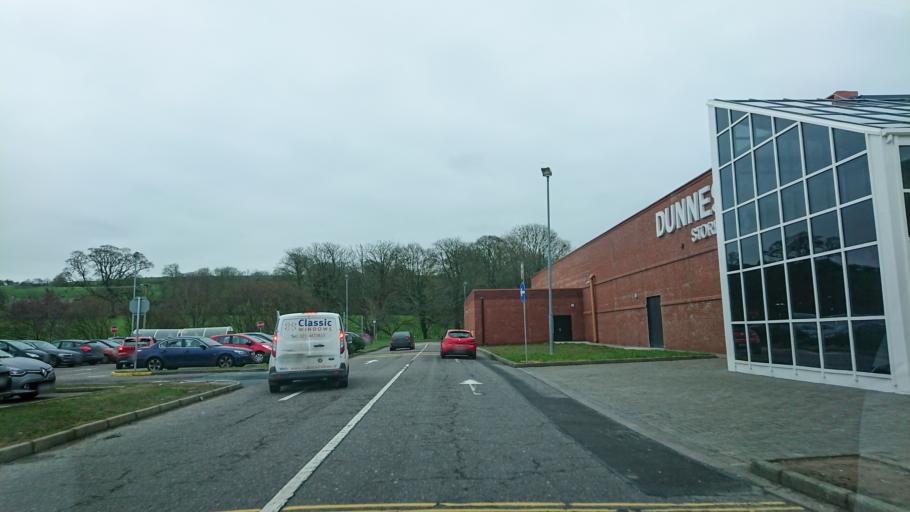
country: IE
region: Munster
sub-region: County Cork
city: Cork
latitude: 51.8741
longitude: -8.5198
